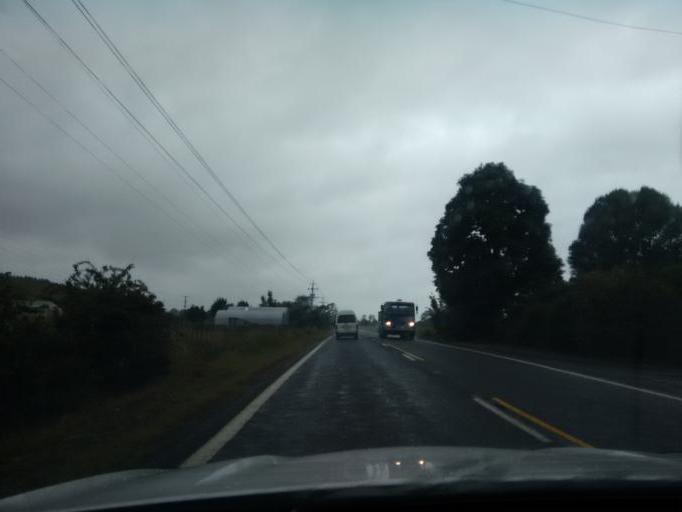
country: NZ
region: Waikato
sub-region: Thames-Coromandel District
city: Whitianga
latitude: -36.8570
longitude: 175.6498
